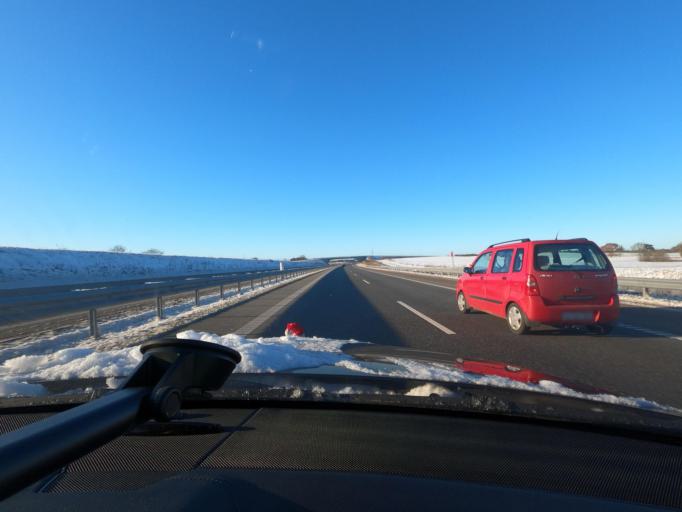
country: DK
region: South Denmark
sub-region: Aabenraa Kommune
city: Krusa
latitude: 54.9432
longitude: 9.4045
